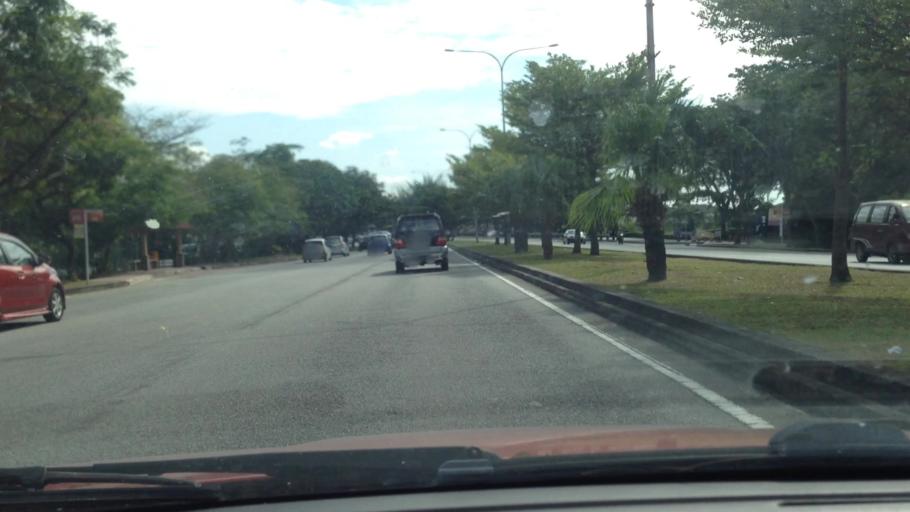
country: MY
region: Selangor
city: Subang Jaya
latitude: 3.0591
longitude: 101.5793
